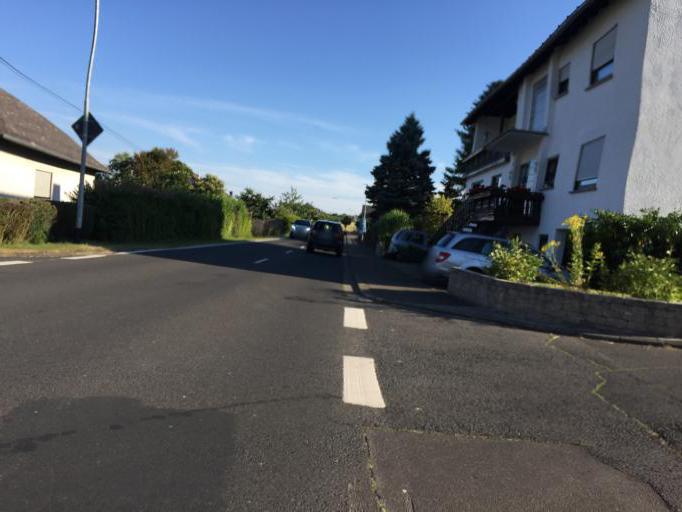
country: DE
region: Rheinland-Pfalz
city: Kaden
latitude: 50.5471
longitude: 7.9136
